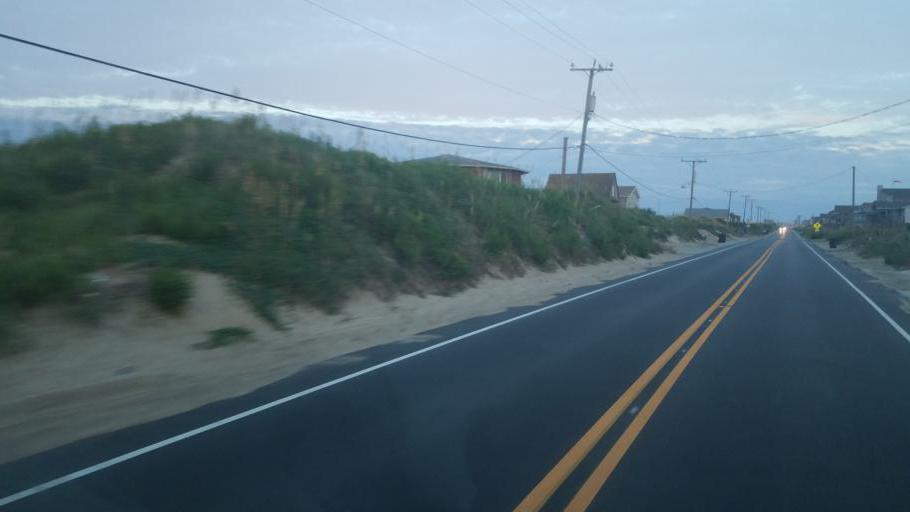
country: US
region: North Carolina
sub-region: Dare County
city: Kitty Hawk
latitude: 36.0622
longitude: -75.6873
